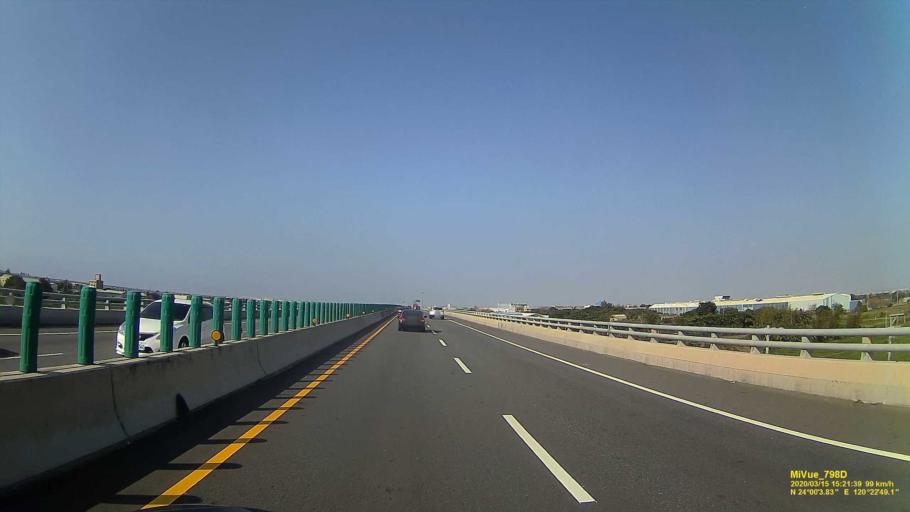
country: TW
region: Taiwan
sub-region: Changhua
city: Chang-hua
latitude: 24.0014
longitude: 120.3805
